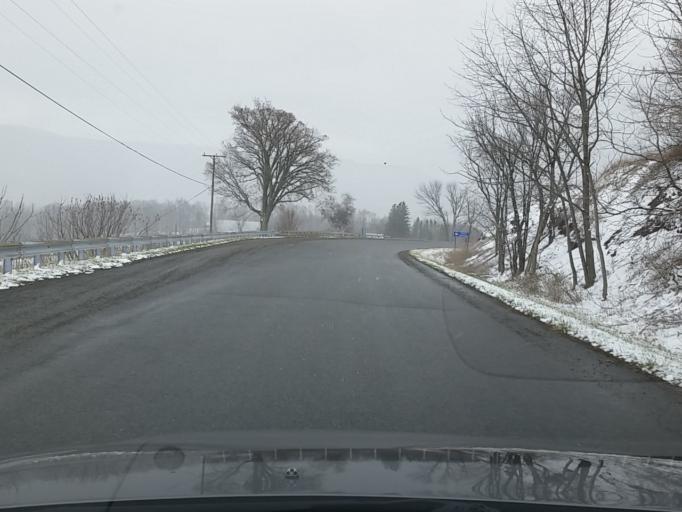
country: US
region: Pennsylvania
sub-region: Sullivan County
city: Laporte
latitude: 41.3789
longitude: -76.5156
